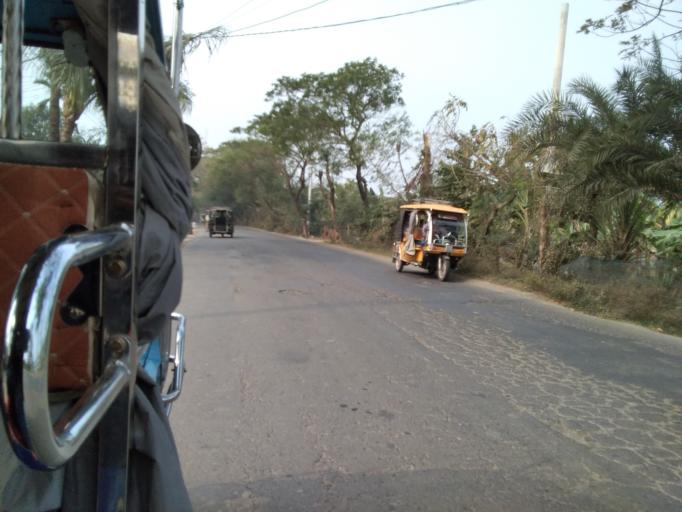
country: BD
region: Khulna
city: Satkhira
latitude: 22.6904
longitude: 89.0383
